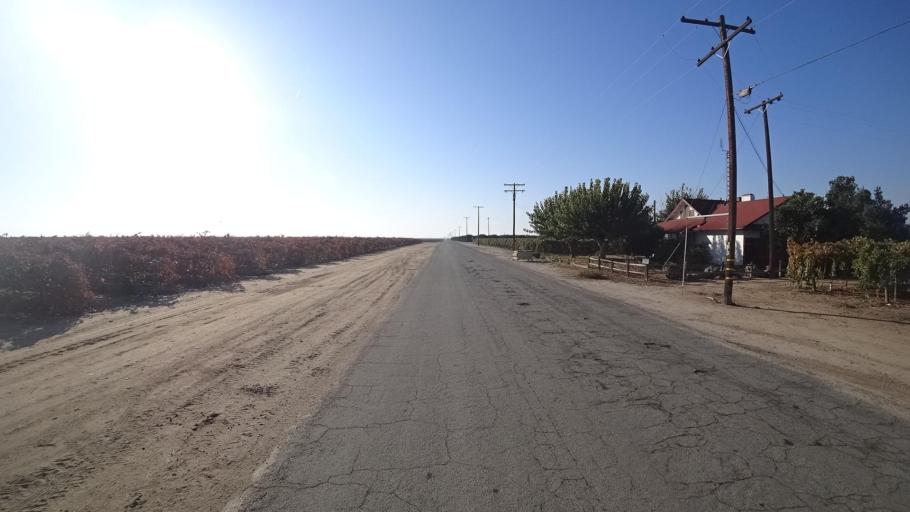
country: US
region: California
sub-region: Tulare County
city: Richgrove
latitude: 35.7702
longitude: -119.1518
